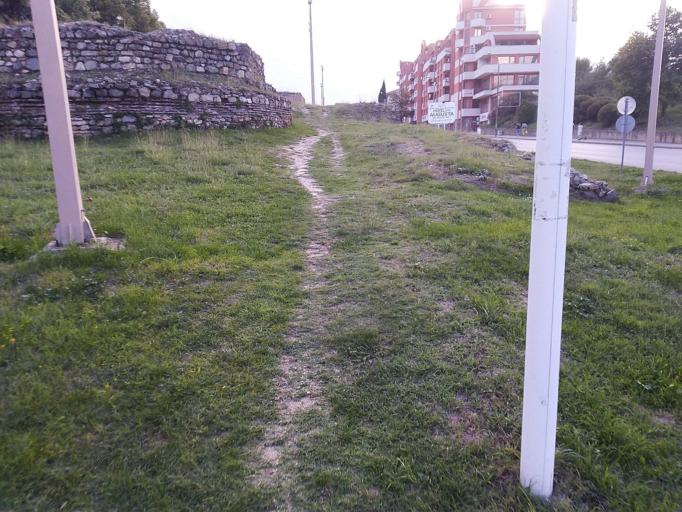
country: BG
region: Plovdiv
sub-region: Obshtina Khisarya
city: Khisarya
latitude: 42.5050
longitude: 24.7056
